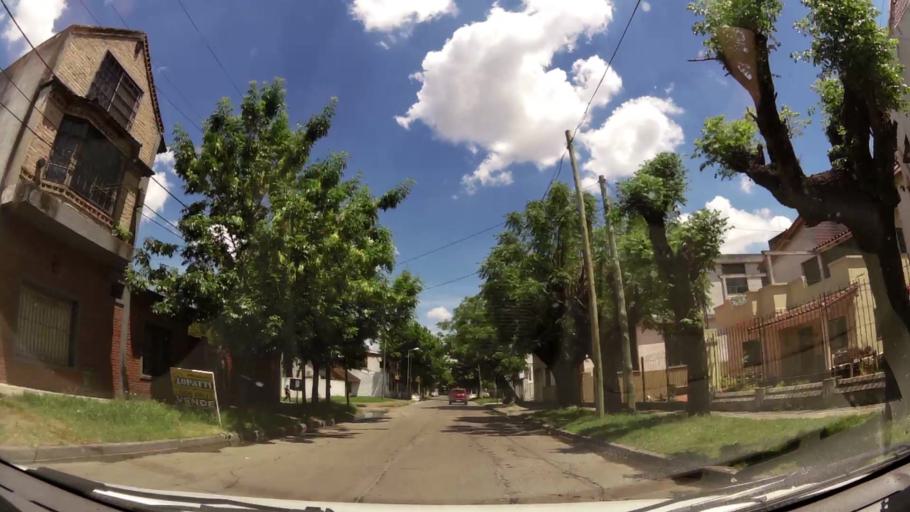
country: AR
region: Buenos Aires
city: Ituzaingo
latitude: -34.6436
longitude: -58.6895
